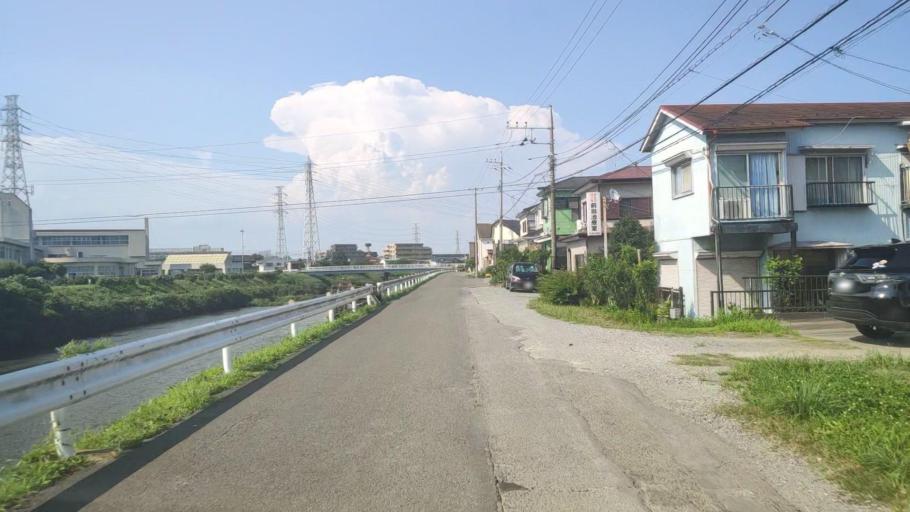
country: JP
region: Kanagawa
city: Hiratsuka
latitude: 35.3465
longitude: 139.3251
